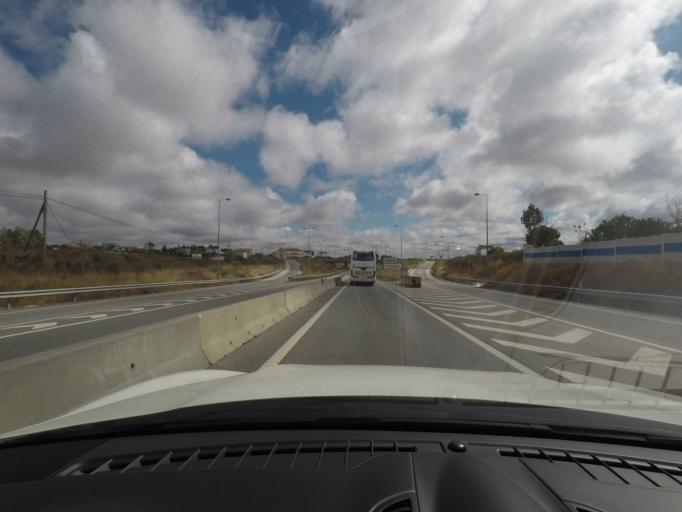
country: ES
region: Castille and Leon
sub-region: Provincia de Salamanca
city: Fuentes de Onoro
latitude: 40.6189
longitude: -6.8455
